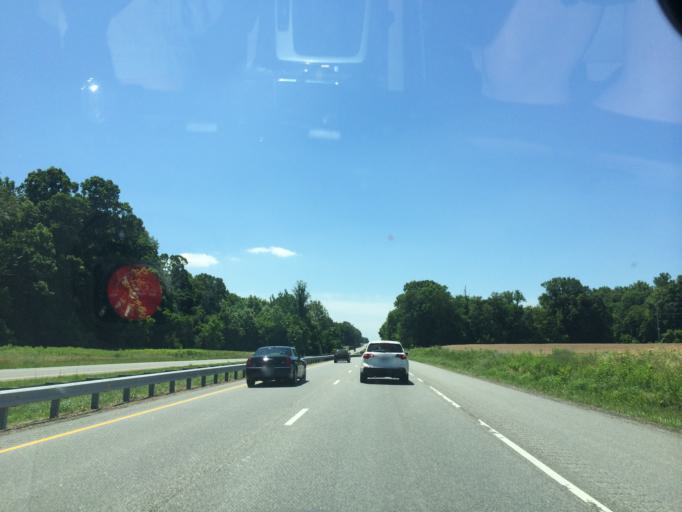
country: US
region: Maryland
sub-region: Talbot County
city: Easton
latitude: 38.8573
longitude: -76.0610
